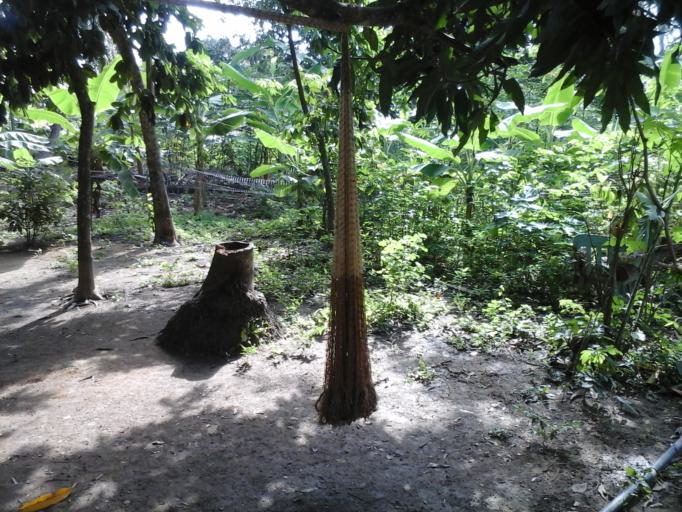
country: CO
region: Cordoba
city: Cotorra
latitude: 9.0832
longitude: -75.7580
